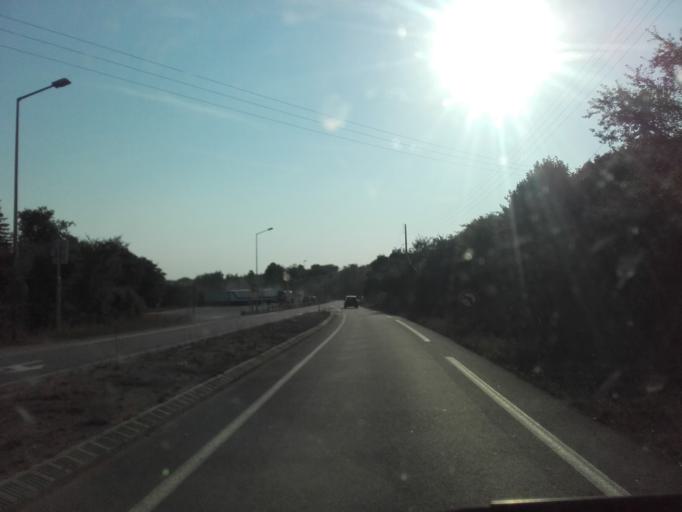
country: FR
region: Bourgogne
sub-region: Departement de l'Yonne
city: Augy
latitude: 47.7909
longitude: 3.6052
